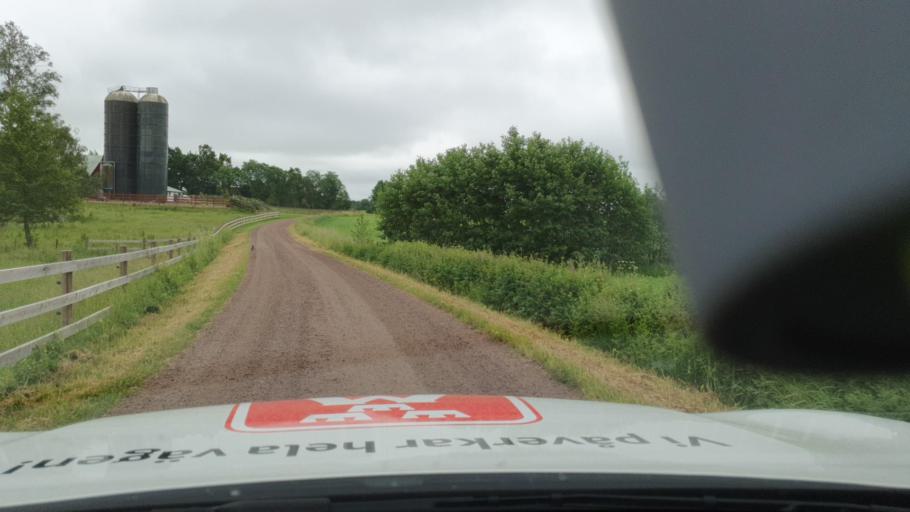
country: SE
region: Vaestra Goetaland
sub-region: Tidaholms Kommun
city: Olofstorp
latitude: 58.3963
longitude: 13.9987
